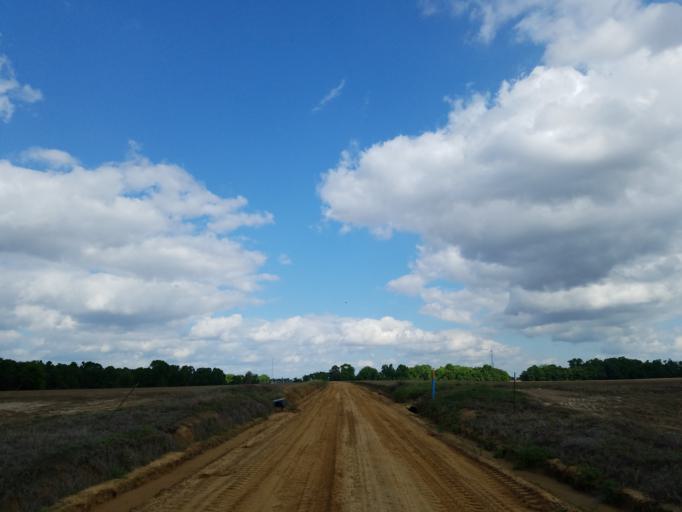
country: US
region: Georgia
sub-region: Dooly County
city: Vienna
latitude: 32.1762
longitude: -83.7798
